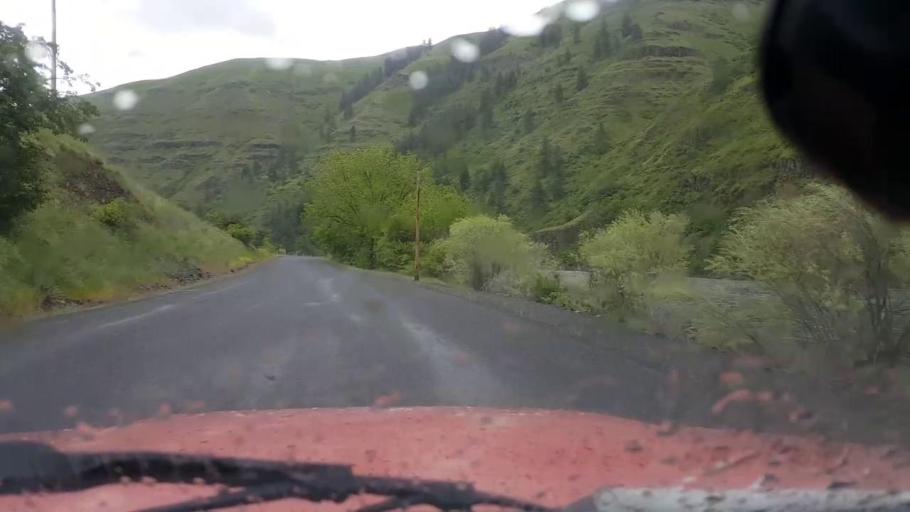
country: US
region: Washington
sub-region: Asotin County
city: Asotin
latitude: 46.0359
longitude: -117.2780
